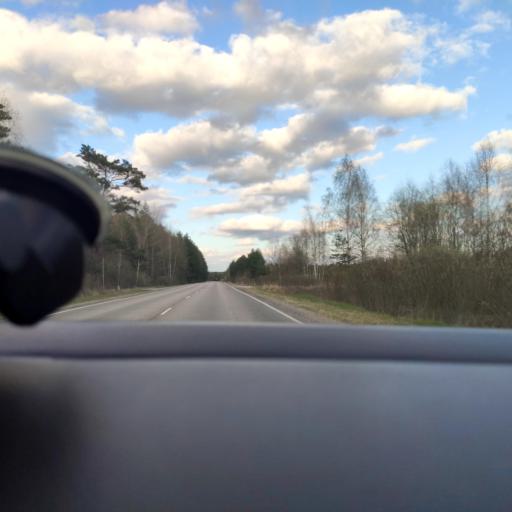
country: RU
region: Moskovskaya
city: Shaturtorf
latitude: 55.4280
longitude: 39.3347
